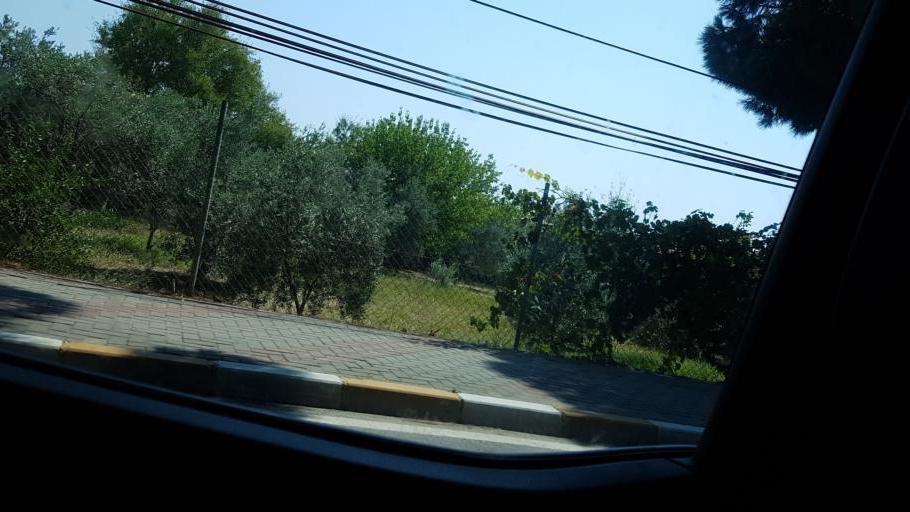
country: TR
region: Izmir
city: Urla
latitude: 38.3615
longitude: 26.7719
